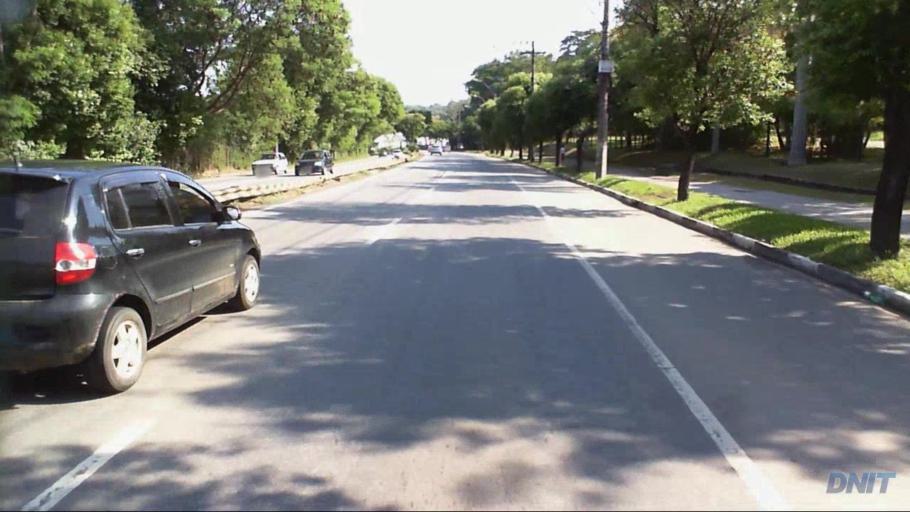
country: BR
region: Minas Gerais
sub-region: Ipatinga
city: Ipatinga
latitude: -19.4886
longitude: -42.5601
